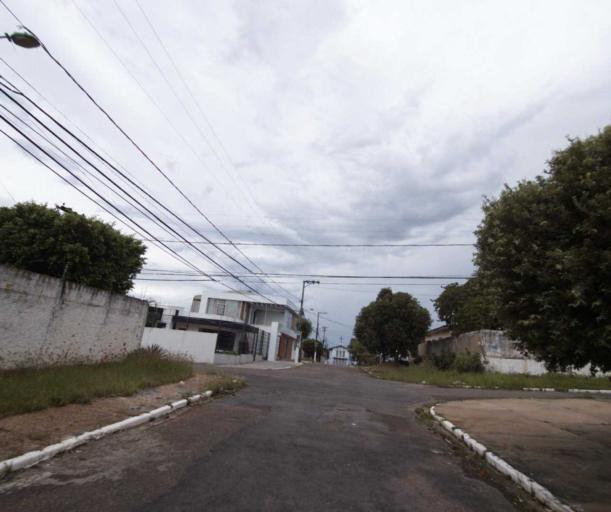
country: BR
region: Mato Grosso
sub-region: Cuiaba
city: Cuiaba
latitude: -15.6042
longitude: -56.0820
